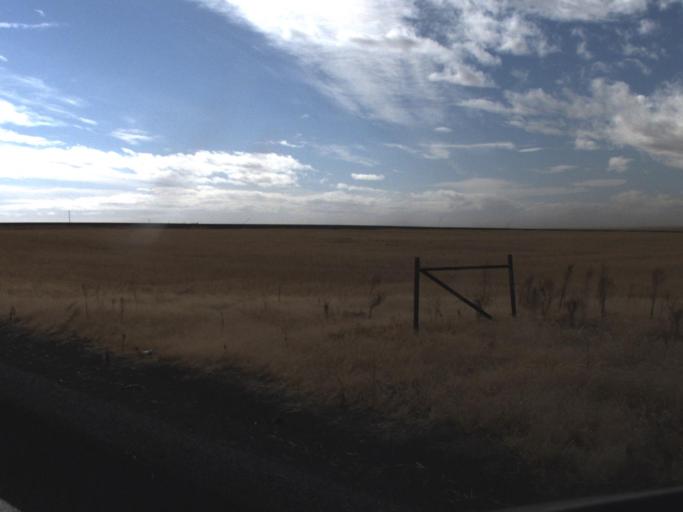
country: US
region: Washington
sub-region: Okanogan County
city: Coulee Dam
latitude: 47.8092
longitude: -118.7218
